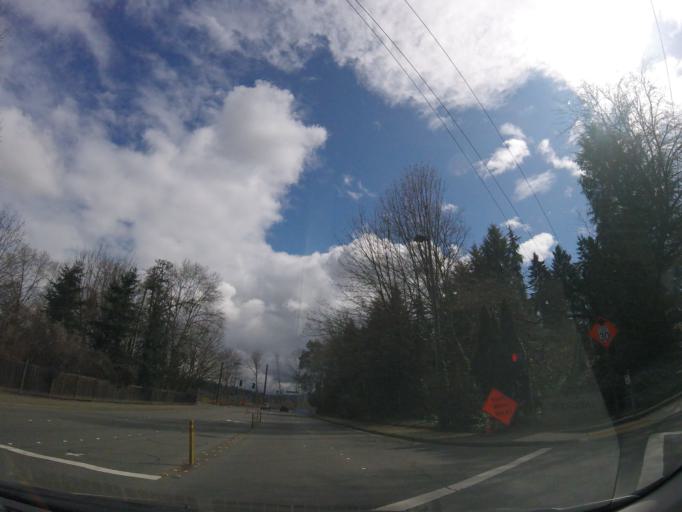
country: US
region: Washington
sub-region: King County
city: Bellevue
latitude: 47.5947
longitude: -122.1969
